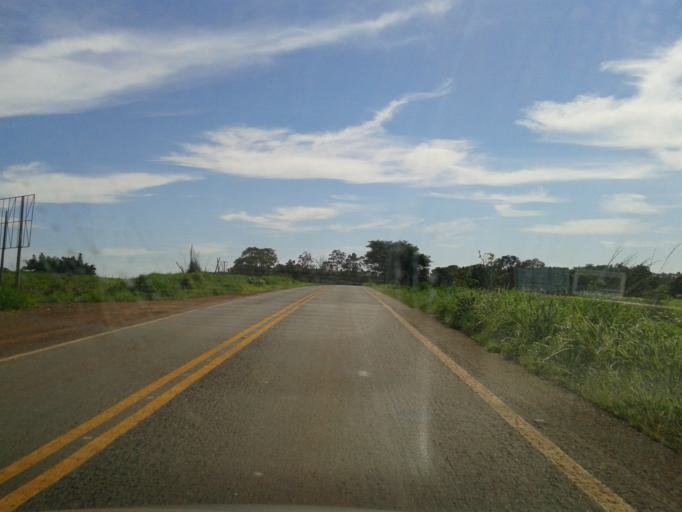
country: BR
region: Goias
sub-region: Piracanjuba
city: Piracanjuba
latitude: -17.2321
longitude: -48.7167
